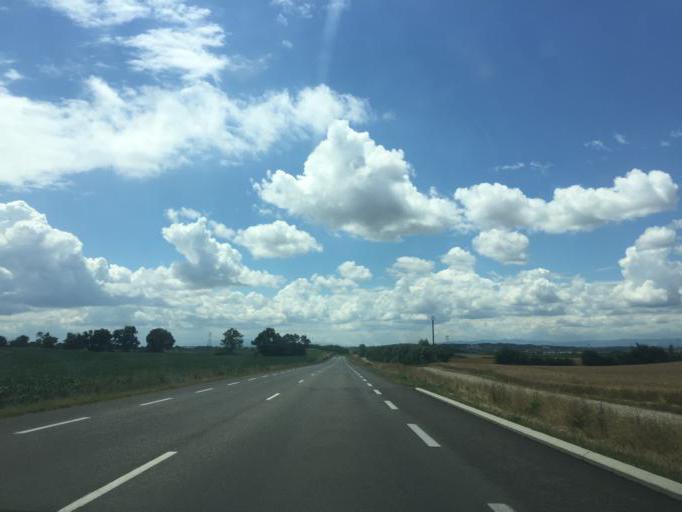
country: FR
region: Rhone-Alpes
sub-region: Departement de l'Isere
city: Janneyrias
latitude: 45.7712
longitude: 5.1258
